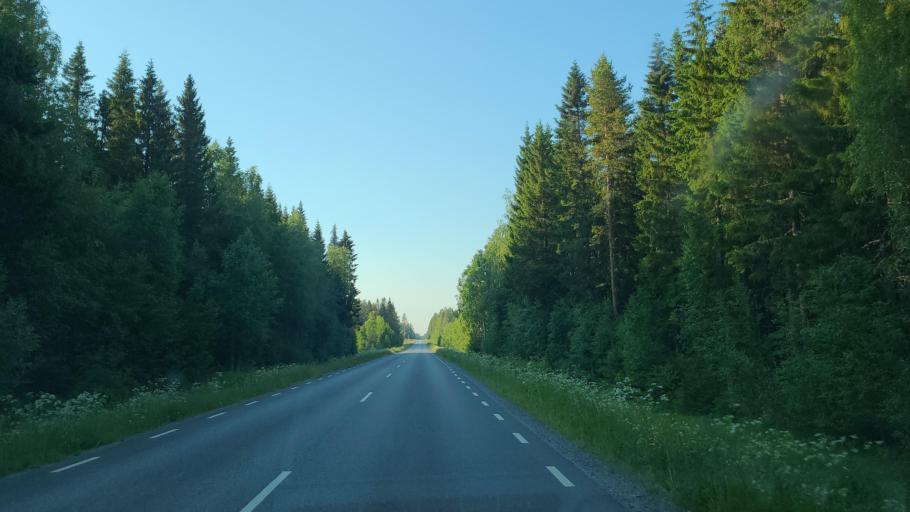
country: SE
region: Vaesterbotten
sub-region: Skelleftea Kommun
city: Burea
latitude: 64.4265
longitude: 21.3533
